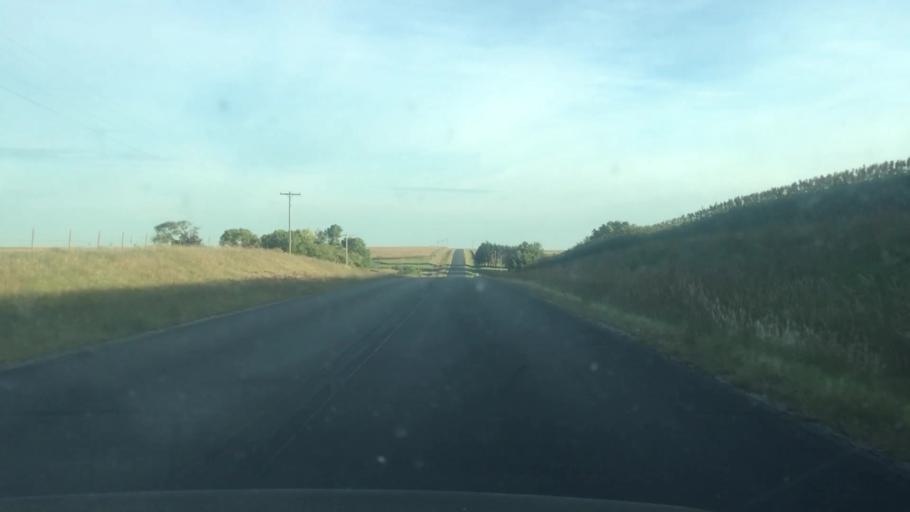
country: US
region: Kansas
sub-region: Marshall County
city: Marysville
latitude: 39.8975
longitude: -96.6010
